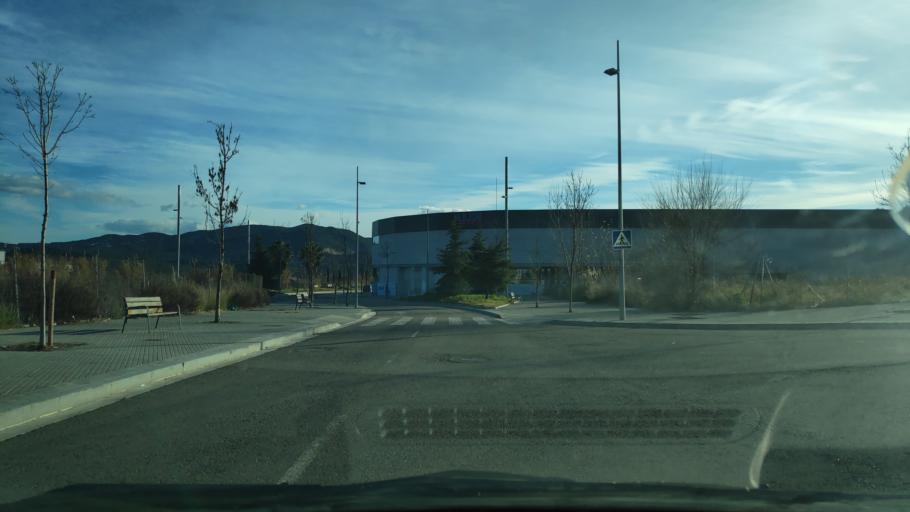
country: ES
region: Catalonia
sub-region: Provincia de Barcelona
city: Mollet del Valles
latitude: 41.5357
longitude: 2.2050
